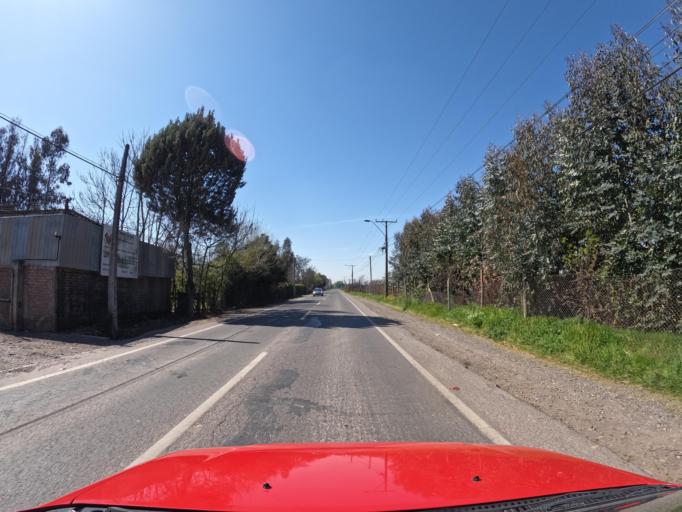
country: CL
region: Maule
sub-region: Provincia de Curico
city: Rauco
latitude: -34.9962
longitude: -71.3622
